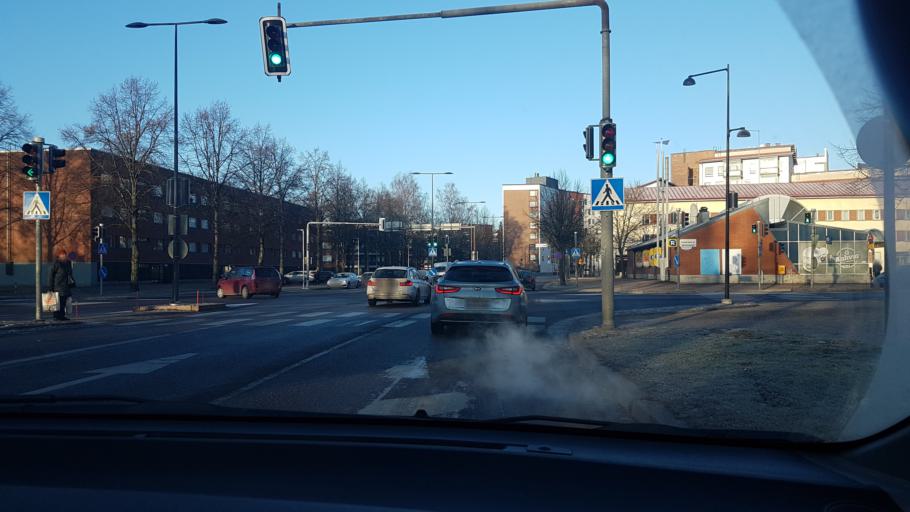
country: FI
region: Uusimaa
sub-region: Helsinki
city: Kerava
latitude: 60.4015
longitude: 25.0987
